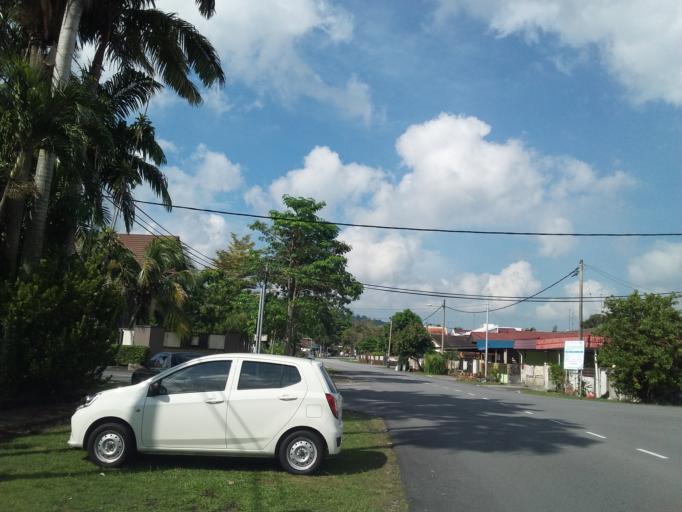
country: MY
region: Johor
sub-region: Daerah Batu Pahat
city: Batu Pahat
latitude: 1.8410
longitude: 102.9299
